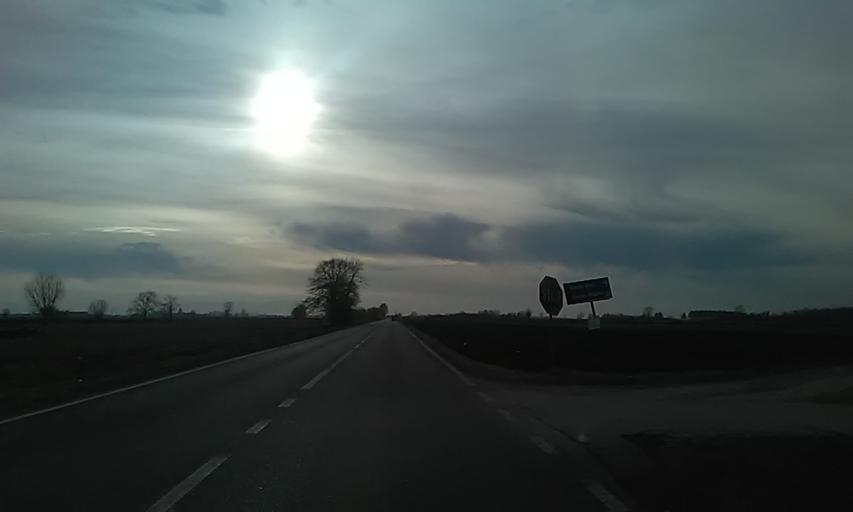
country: IT
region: Piedmont
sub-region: Provincia di Torino
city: Villareggia
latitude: 45.2914
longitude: 7.9988
